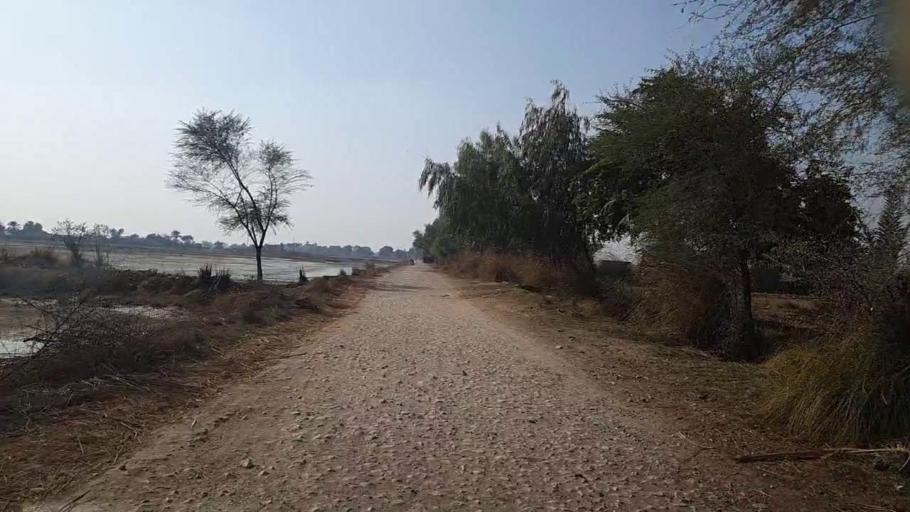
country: PK
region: Sindh
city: Mirpur Mathelo
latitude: 27.9028
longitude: 69.6291
